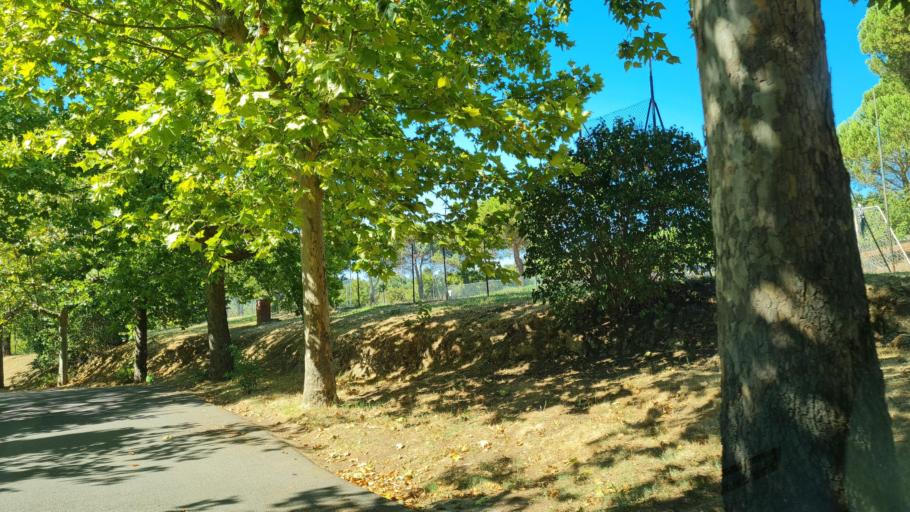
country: IT
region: Tuscany
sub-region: Provincia di Siena
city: Chianciano Terme
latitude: 43.0403
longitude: 11.8100
